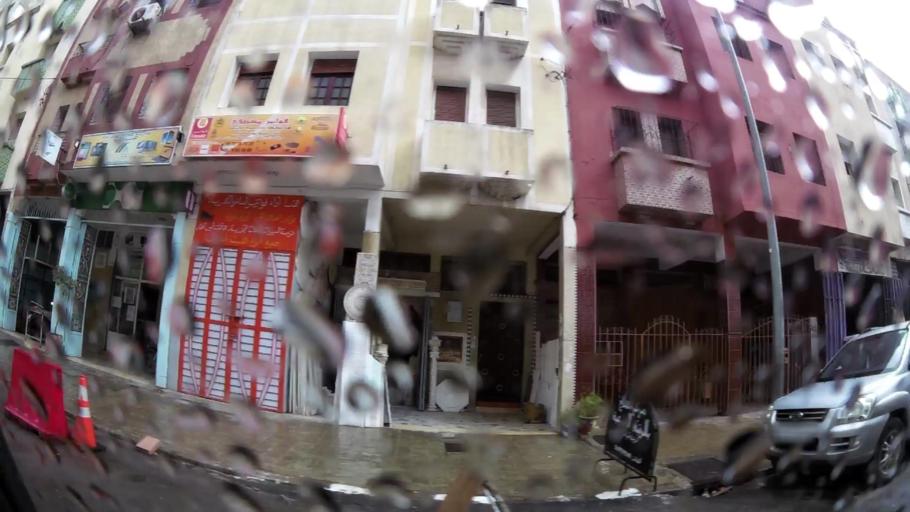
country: MA
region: Grand Casablanca
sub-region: Mediouna
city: Tit Mellil
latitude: 33.6157
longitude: -7.4934
